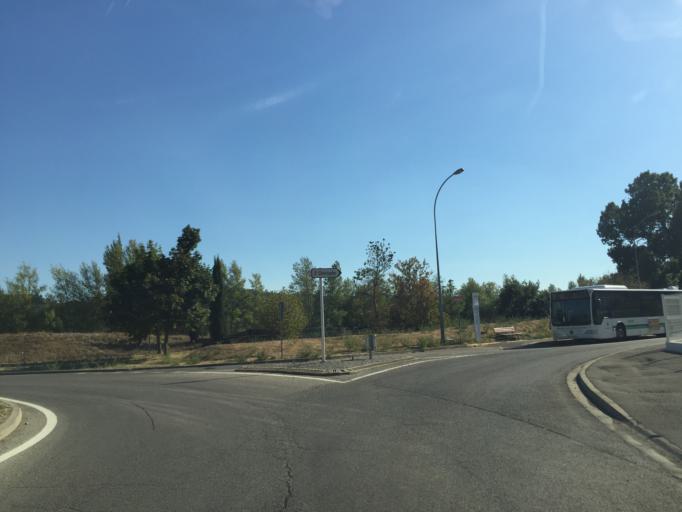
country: FR
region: Provence-Alpes-Cote d'Azur
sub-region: Departement des Alpes-de-Haute-Provence
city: Digne-les-Bains
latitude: 44.0784
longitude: 6.1946
